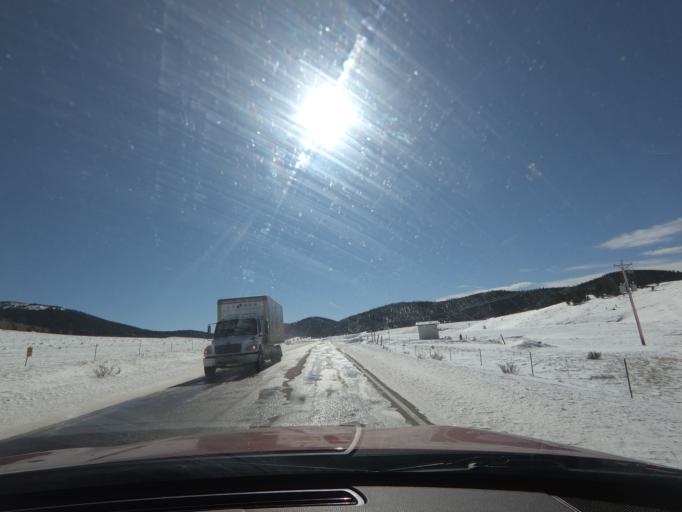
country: US
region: Colorado
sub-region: Teller County
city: Cripple Creek
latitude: 38.7696
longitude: -105.1190
